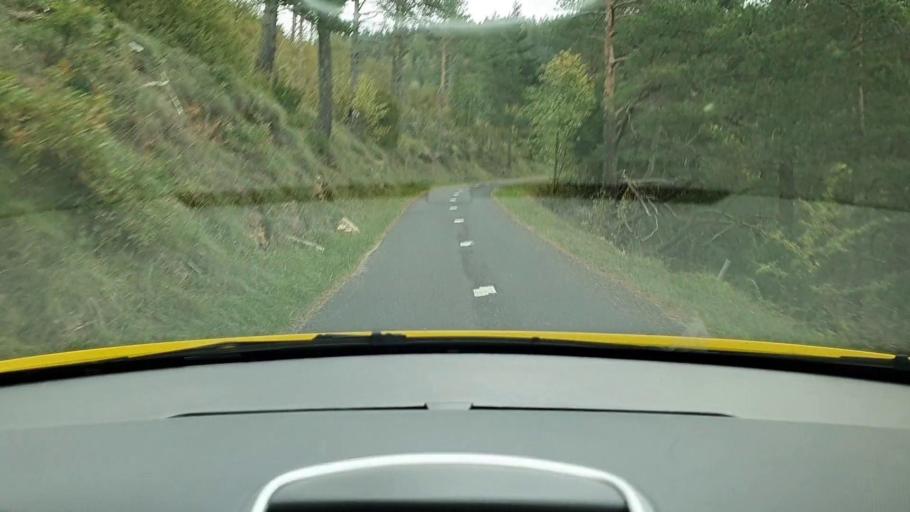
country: FR
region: Languedoc-Roussillon
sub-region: Departement de la Lozere
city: Meyrueis
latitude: 44.1256
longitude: 3.4326
